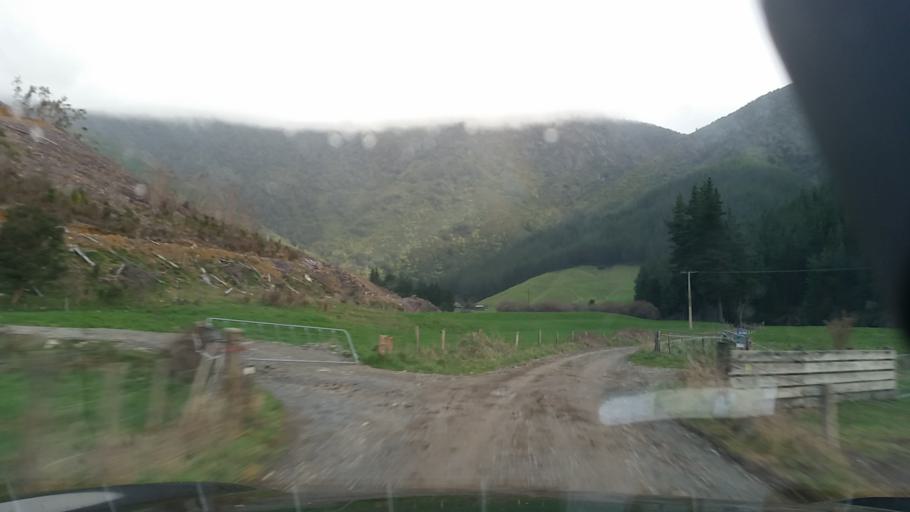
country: NZ
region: Marlborough
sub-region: Marlborough District
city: Picton
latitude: -41.2113
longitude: 173.6951
